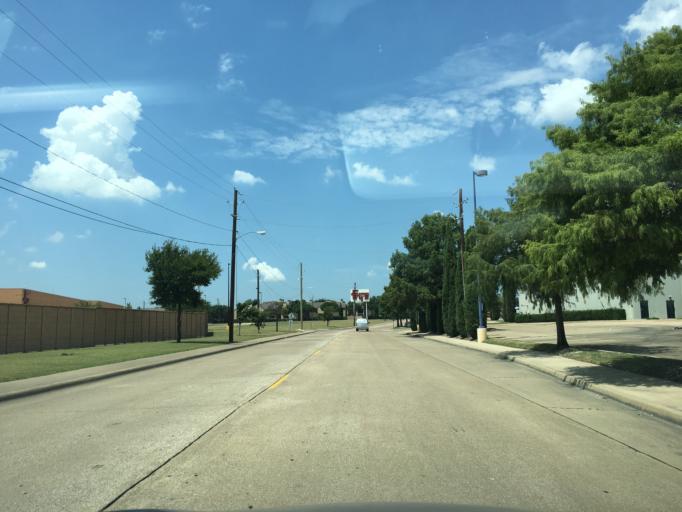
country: US
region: Texas
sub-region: Dallas County
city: Garland
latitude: 32.8689
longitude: -96.6751
